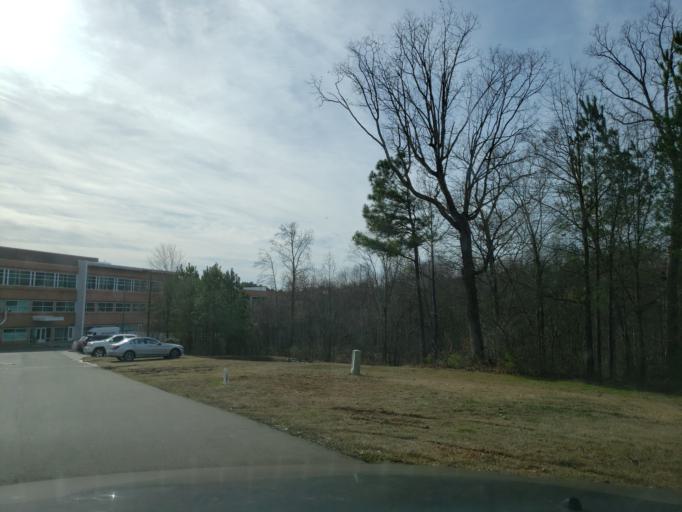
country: US
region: North Carolina
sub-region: Durham County
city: Durham
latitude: 35.9118
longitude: -78.9290
